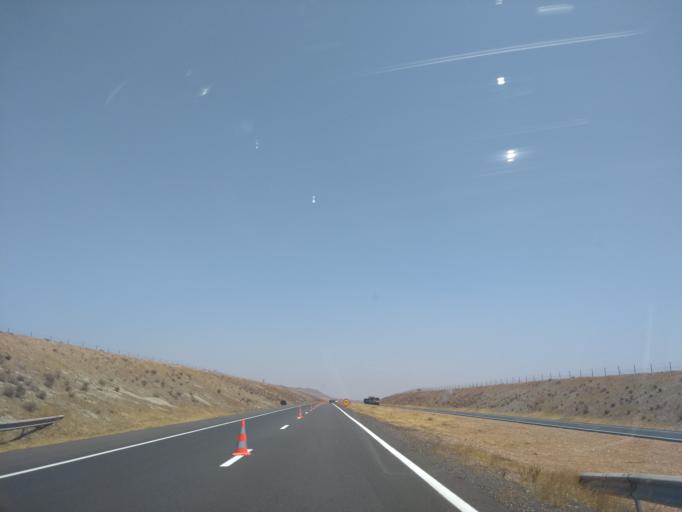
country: MA
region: Marrakech-Tensift-Al Haouz
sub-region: Kelaa-Des-Sraghna
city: Sidi Abdallah
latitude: 32.4379
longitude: -7.9317
